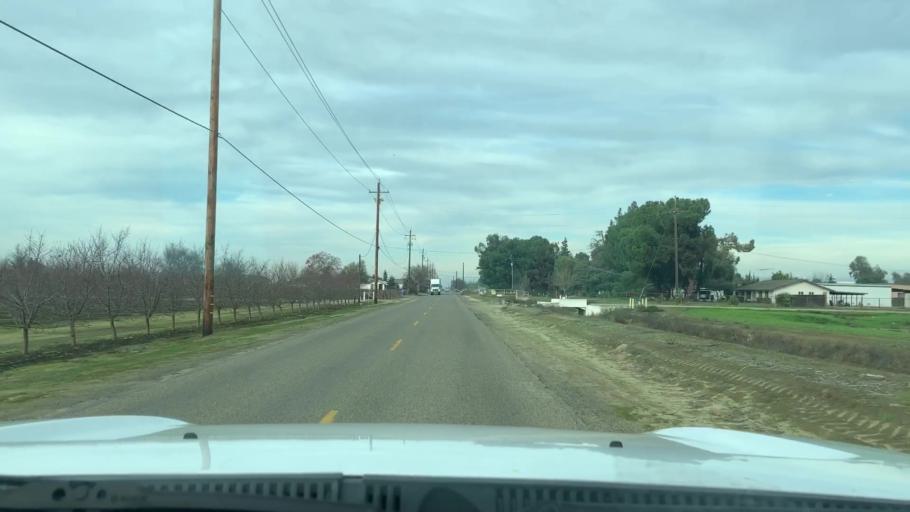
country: US
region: California
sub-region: Fresno County
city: Selma
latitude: 36.5788
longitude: -119.5749
